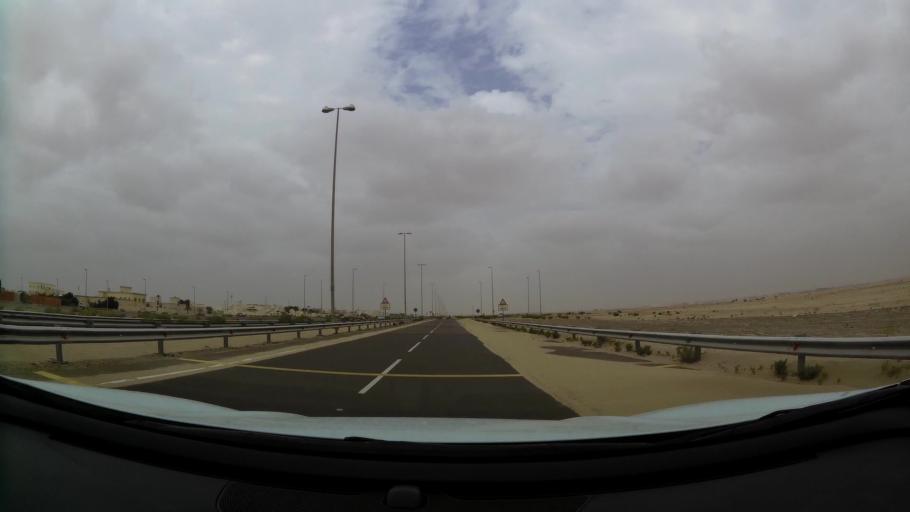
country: AE
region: Abu Dhabi
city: Abu Dhabi
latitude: 24.3454
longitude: 54.6579
